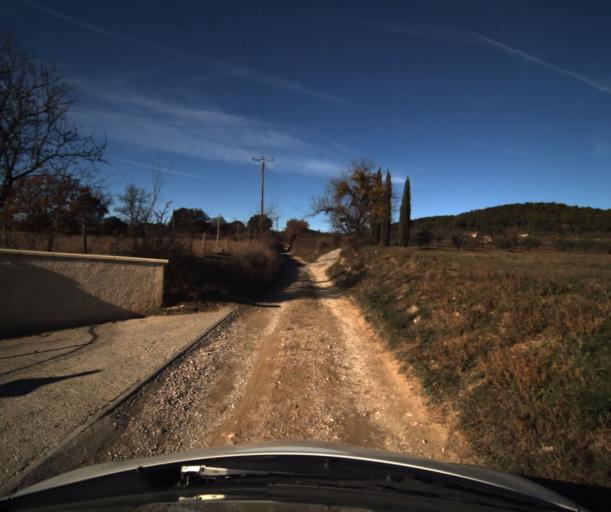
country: FR
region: Provence-Alpes-Cote d'Azur
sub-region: Departement du Vaucluse
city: Pertuis
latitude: 43.7001
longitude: 5.4743
